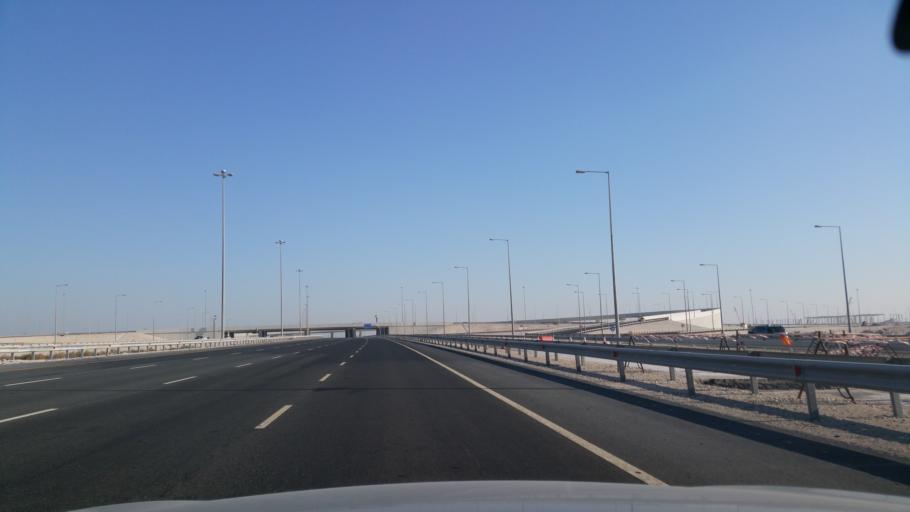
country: QA
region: Al Wakrah
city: Al Wukayr
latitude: 25.1267
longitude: 51.4835
